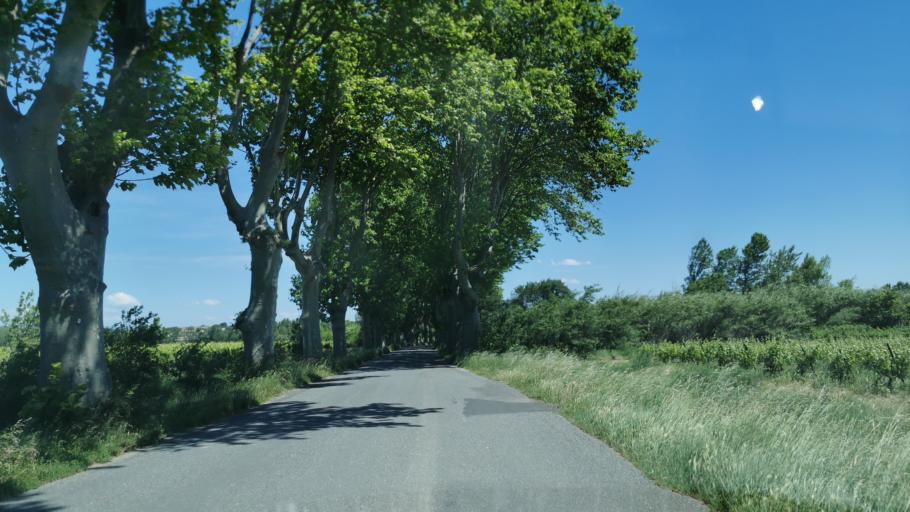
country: FR
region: Languedoc-Roussillon
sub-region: Departement de l'Aude
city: Canet
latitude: 43.2372
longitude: 2.8530
